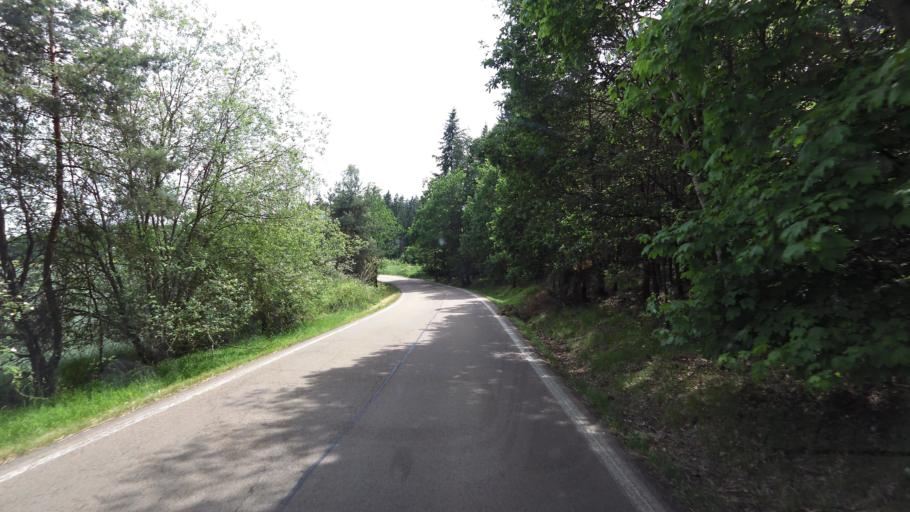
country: CZ
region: Plzensky
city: Stary Plzenec
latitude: 49.6786
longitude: 13.4756
